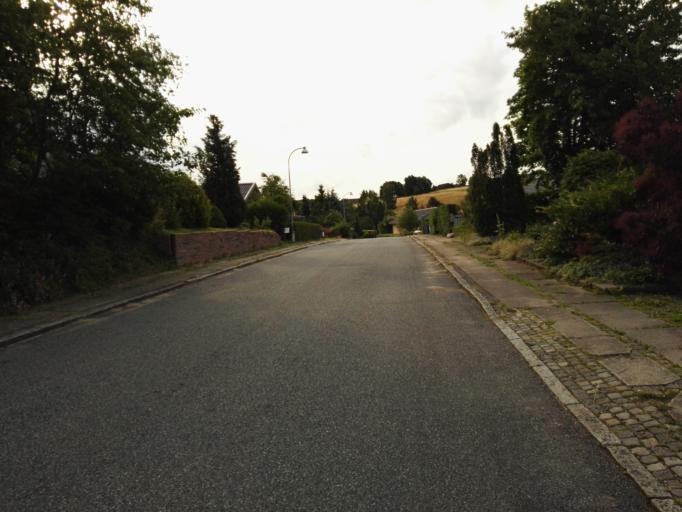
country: DK
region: Capital Region
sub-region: Ballerup Kommune
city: Malov
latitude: 55.7574
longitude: 12.3244
